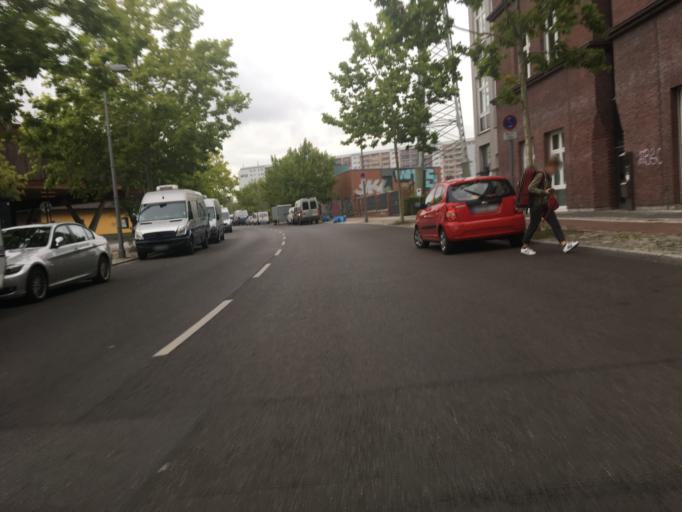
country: DE
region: Berlin
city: Fennpfuhl
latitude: 52.5214
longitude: 13.4695
